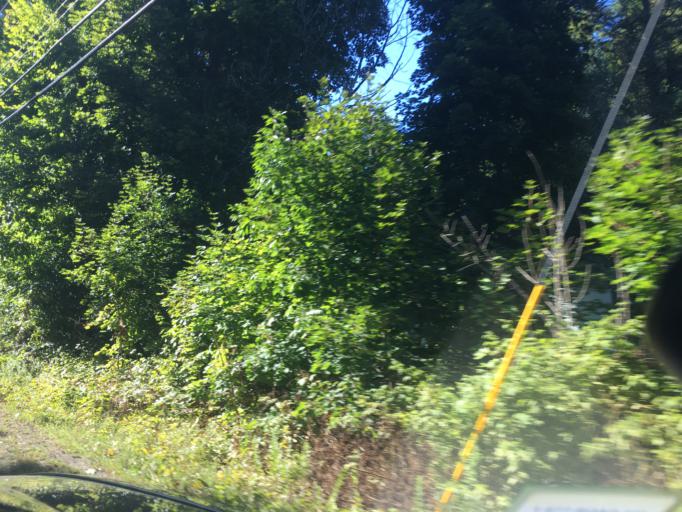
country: US
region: New Hampshire
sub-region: Rockingham County
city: Stratham Station
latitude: 43.0237
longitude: -70.8962
